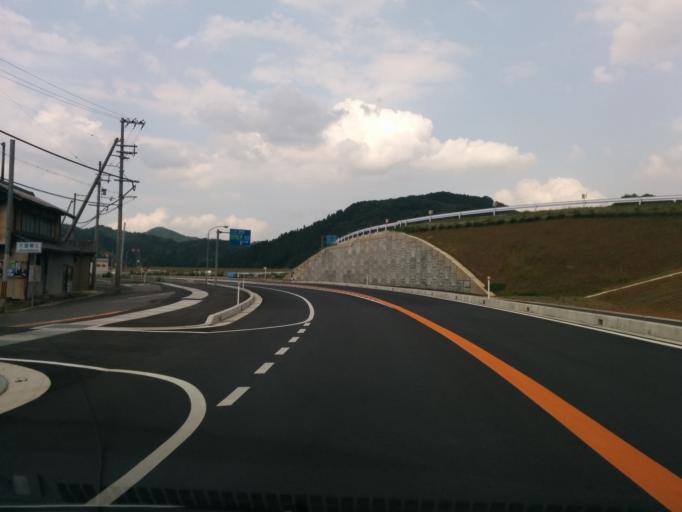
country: JP
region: Kyoto
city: Fukuchiyama
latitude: 35.3924
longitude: 135.1796
